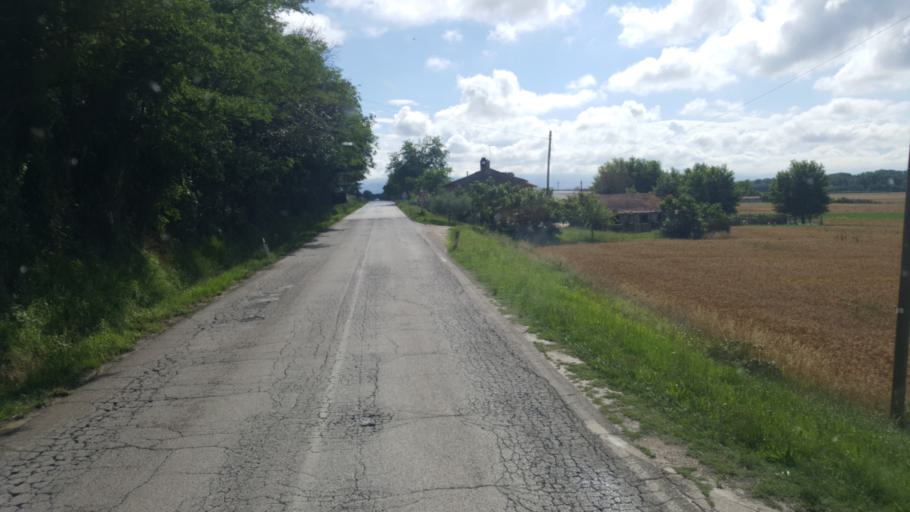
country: IT
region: Umbria
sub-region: Provincia di Perugia
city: Torgiano
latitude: 43.0351
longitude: 12.4472
